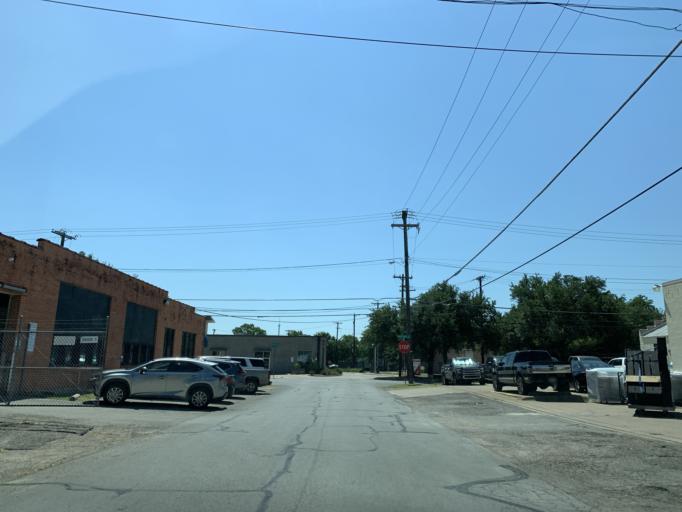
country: US
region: Texas
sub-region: Dallas County
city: Dallas
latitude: 32.7874
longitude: -96.7714
